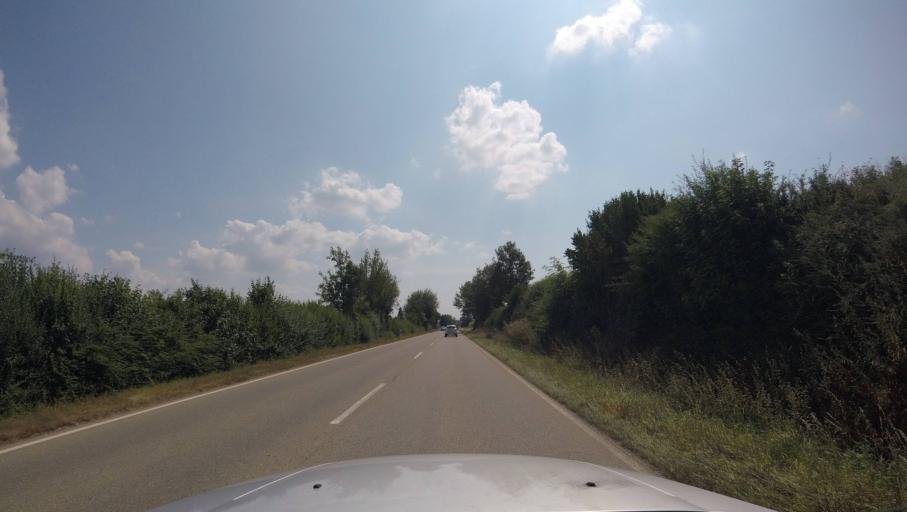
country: DE
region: Baden-Wuerttemberg
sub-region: Regierungsbezirk Stuttgart
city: Welzheim
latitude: 48.9015
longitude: 9.6261
